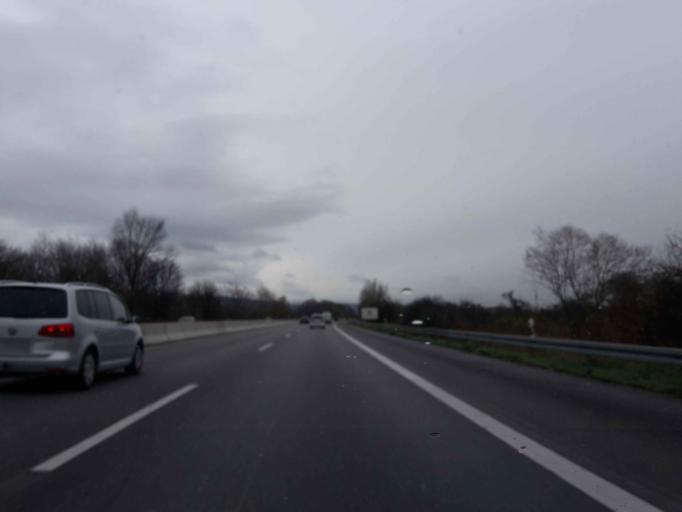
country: DE
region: Hesse
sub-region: Regierungsbezirk Darmstadt
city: Heppenheim an der Bergstrasse
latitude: 49.6170
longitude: 8.6242
